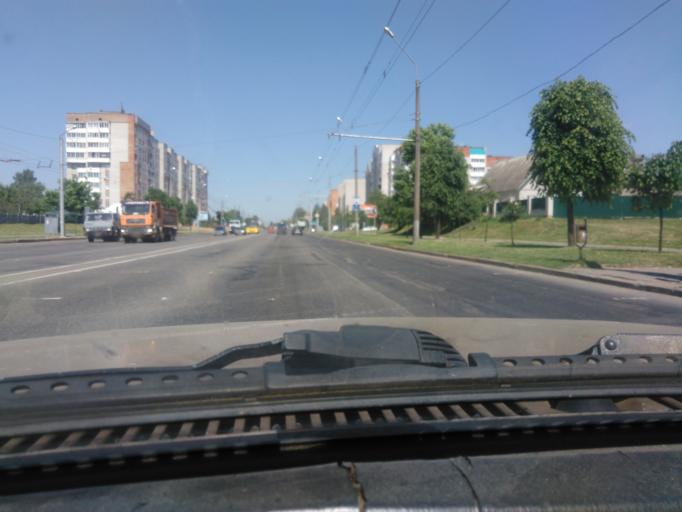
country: BY
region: Mogilev
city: Mahilyow
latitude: 53.9316
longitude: 30.3519
